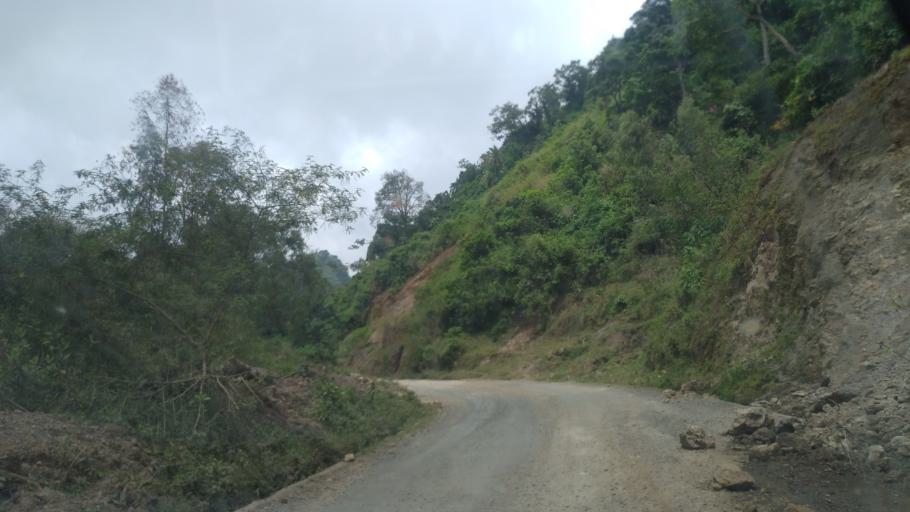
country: ET
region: Southern Nations, Nationalities, and People's Region
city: Bonga
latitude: 7.1126
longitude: 36.7278
